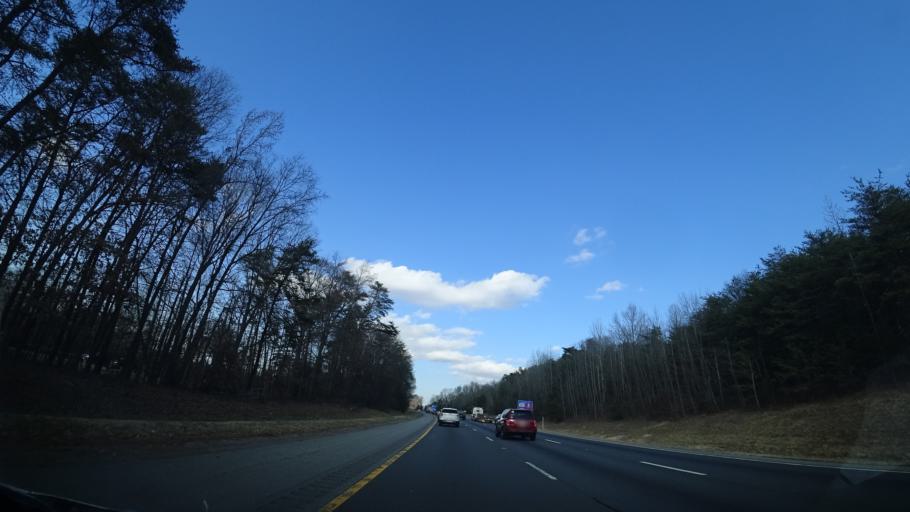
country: US
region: Virginia
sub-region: Spotsylvania County
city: Spotsylvania Courthouse
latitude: 38.2096
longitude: -77.4972
